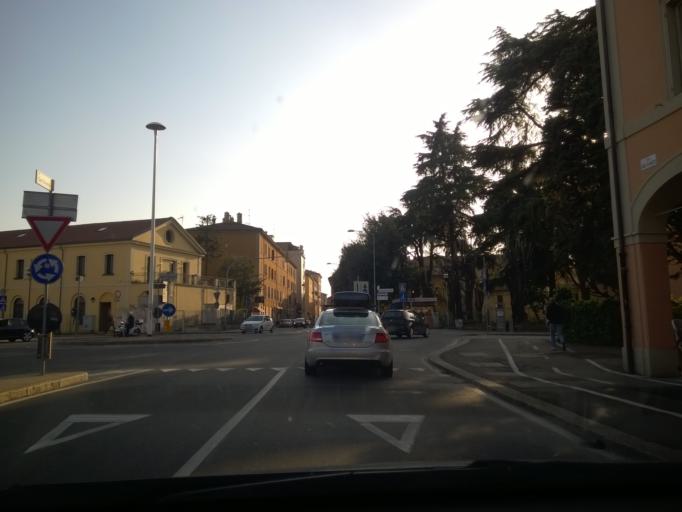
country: IT
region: Emilia-Romagna
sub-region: Provincia di Bologna
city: Bologna
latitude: 44.4998
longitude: 11.3593
